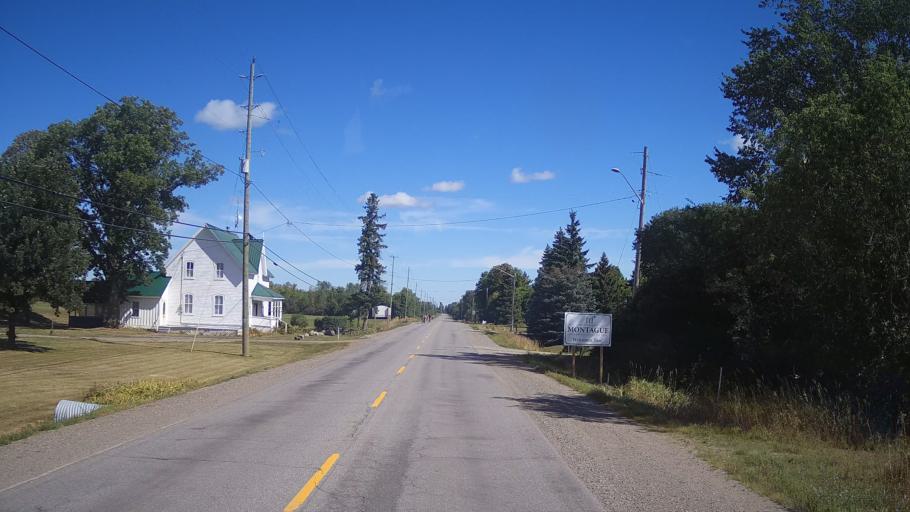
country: CA
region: Ontario
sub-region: Lanark County
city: Smiths Falls
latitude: 44.9253
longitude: -75.8364
